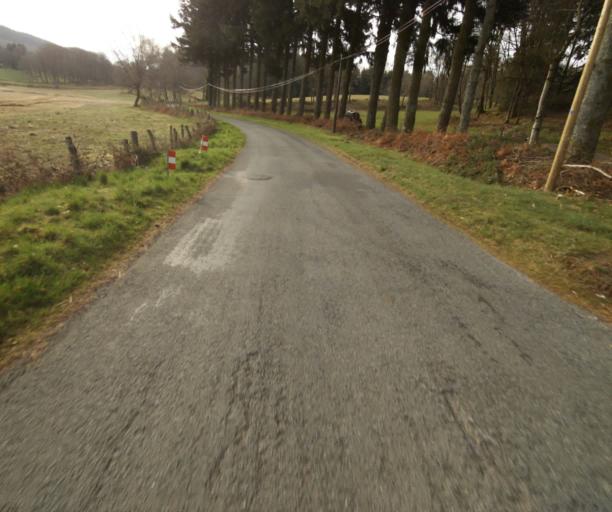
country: FR
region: Limousin
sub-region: Departement de la Correze
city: Treignac
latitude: 45.4680
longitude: 1.8061
